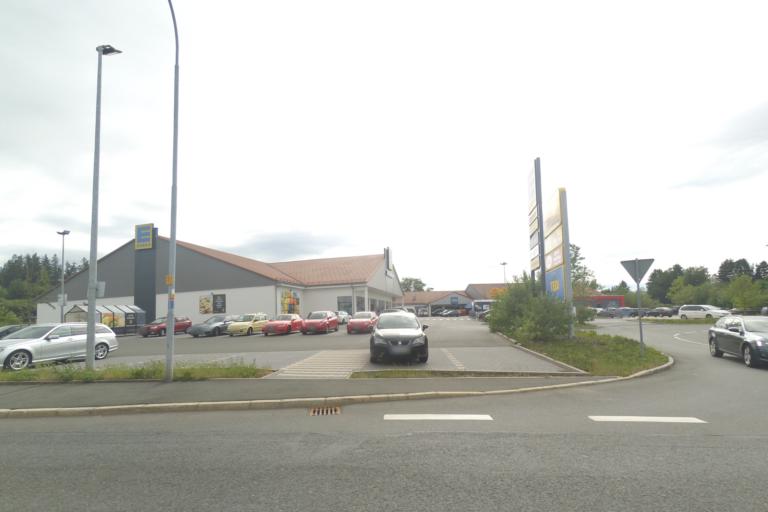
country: DE
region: Bavaria
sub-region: Upper Franconia
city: Munchberg
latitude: 50.1810
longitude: 11.7929
